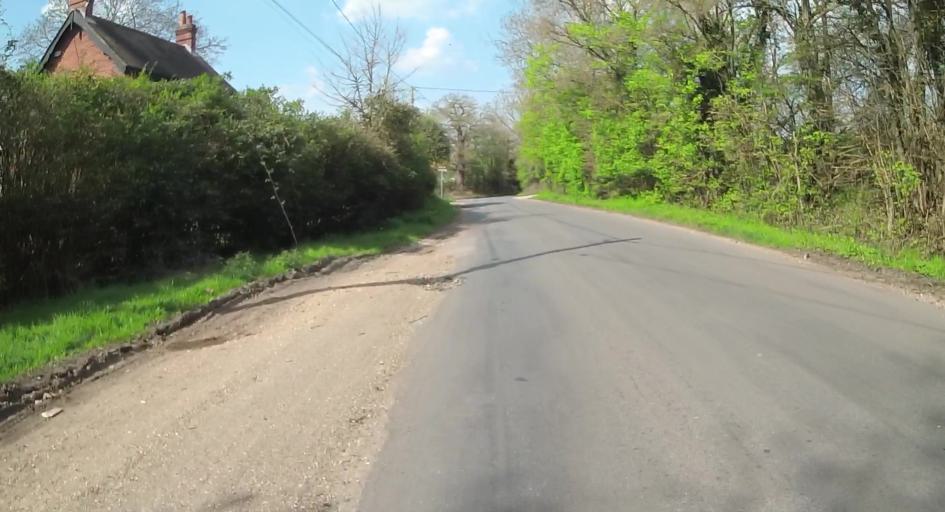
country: GB
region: England
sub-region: Hampshire
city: Tadley
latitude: 51.3752
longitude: -1.1267
